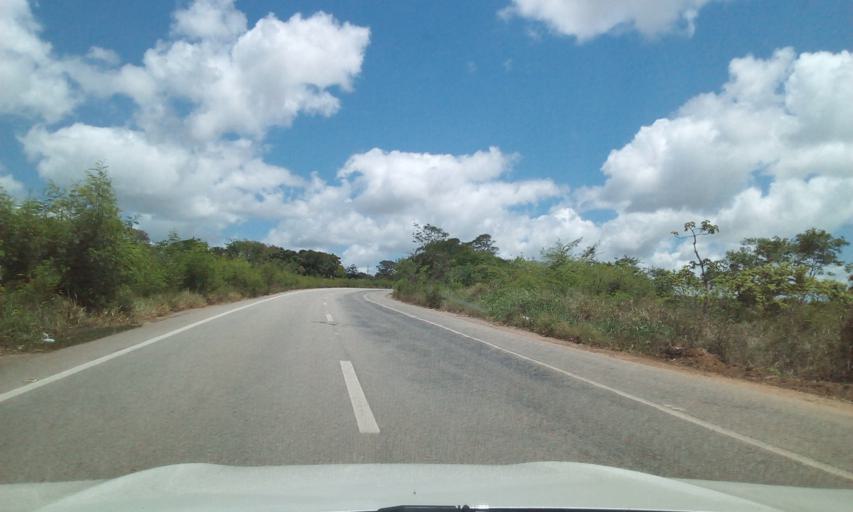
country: BR
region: Alagoas
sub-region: Campo Alegre
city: Campo Alegre
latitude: -9.9082
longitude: -36.3232
